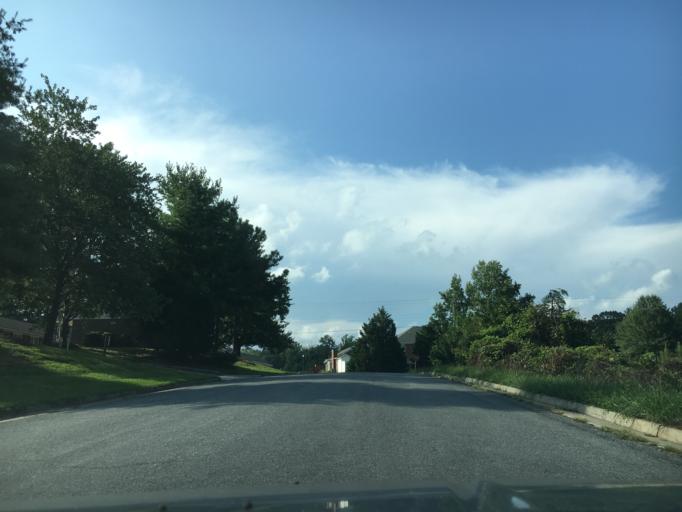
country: US
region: Virginia
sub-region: Halifax County
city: South Boston
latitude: 36.7127
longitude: -78.9174
